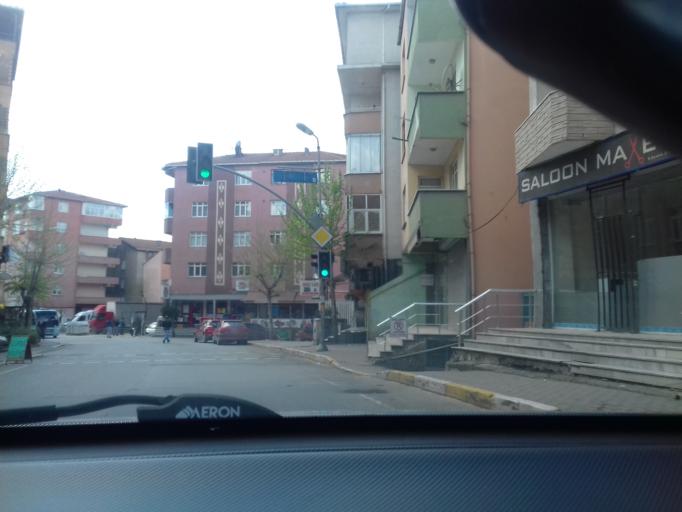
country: TR
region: Istanbul
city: Pendik
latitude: 40.8724
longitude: 29.2811
